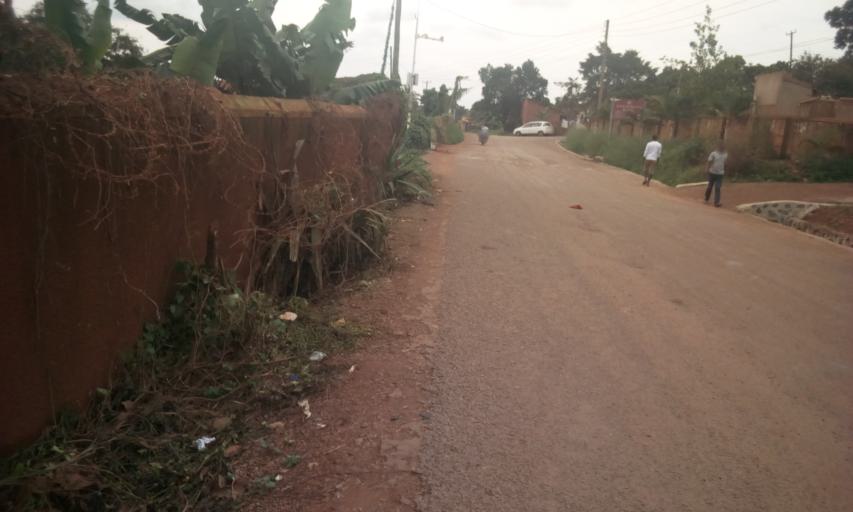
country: UG
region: Central Region
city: Kampala Central Division
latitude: 0.3389
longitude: 32.5612
